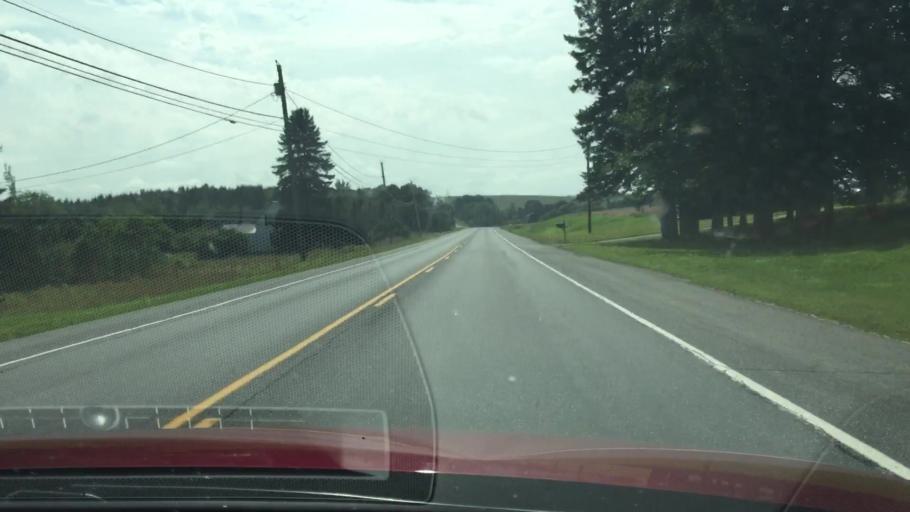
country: US
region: Maine
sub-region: Aroostook County
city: Easton
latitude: 46.5893
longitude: -67.9622
